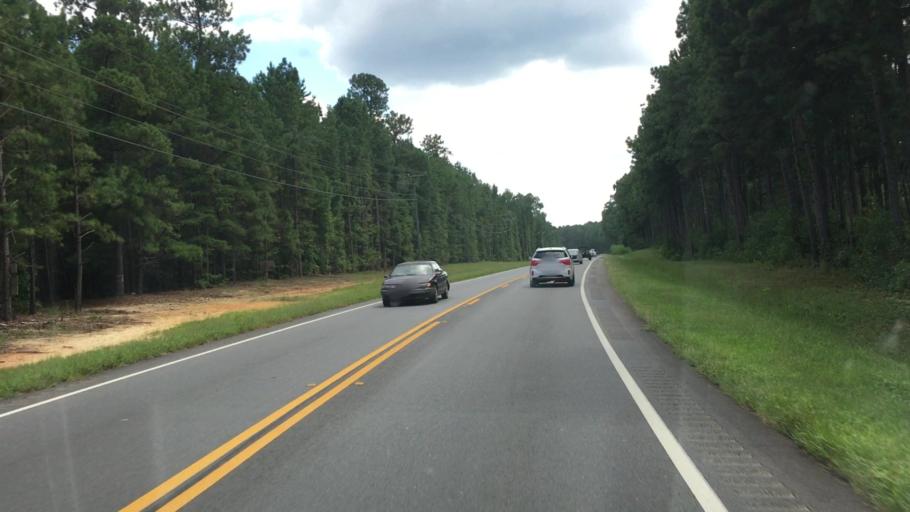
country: US
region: Georgia
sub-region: Putnam County
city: Jefferson
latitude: 33.4046
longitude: -83.3677
